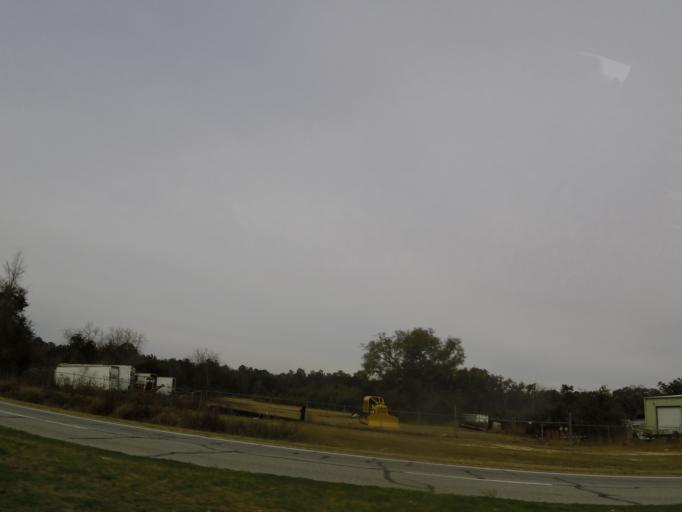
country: US
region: Georgia
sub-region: Decatur County
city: Bainbridge
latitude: 30.9223
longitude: -84.6082
